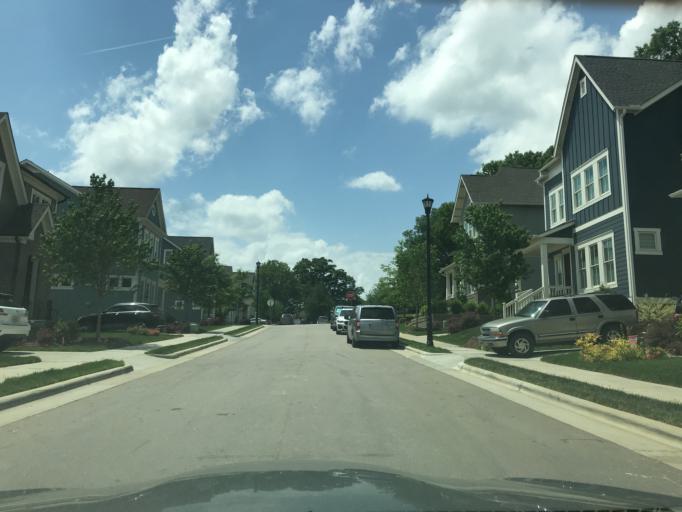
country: US
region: North Carolina
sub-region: Wake County
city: Raleigh
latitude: 35.7923
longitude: -78.6281
